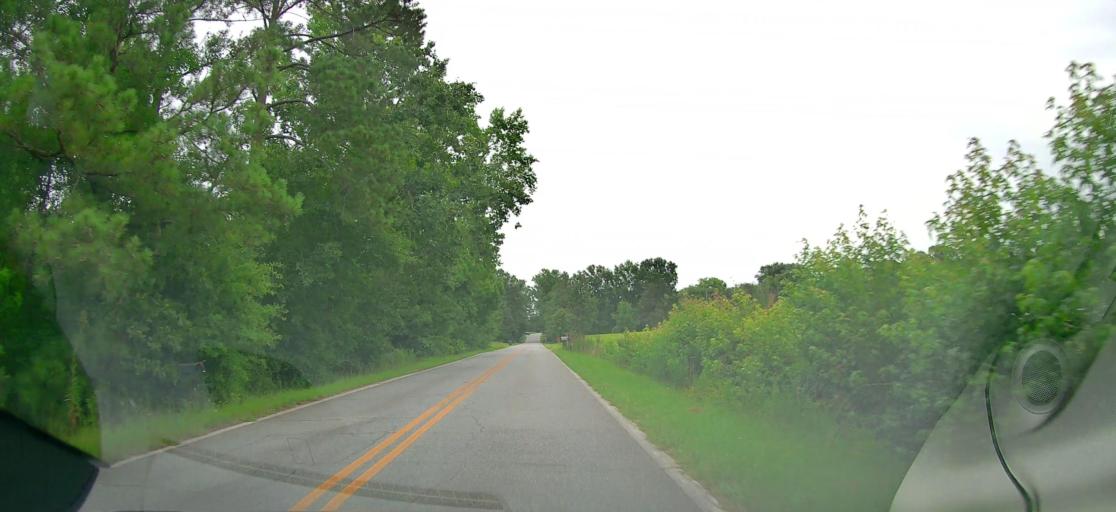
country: US
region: Georgia
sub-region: Bibb County
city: West Point
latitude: 32.7694
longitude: -83.7807
